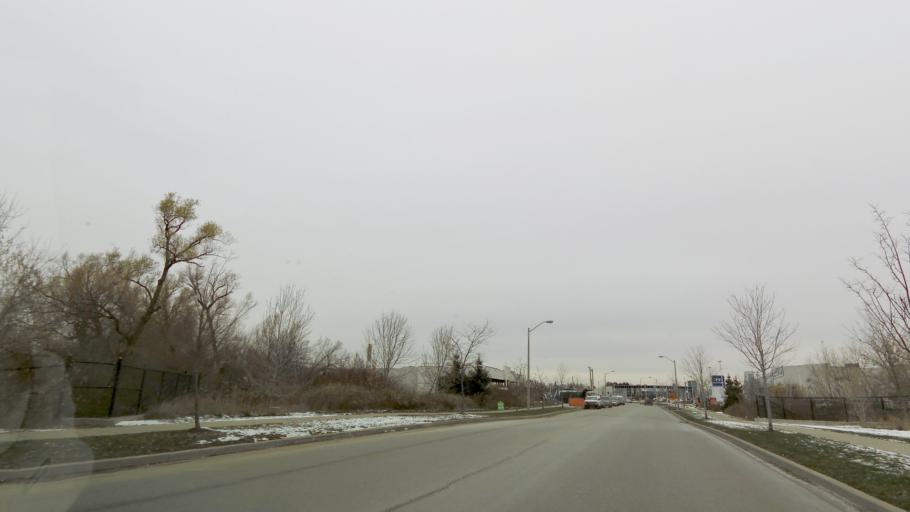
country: CA
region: Ontario
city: Vaughan
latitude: 43.8339
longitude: -79.5382
